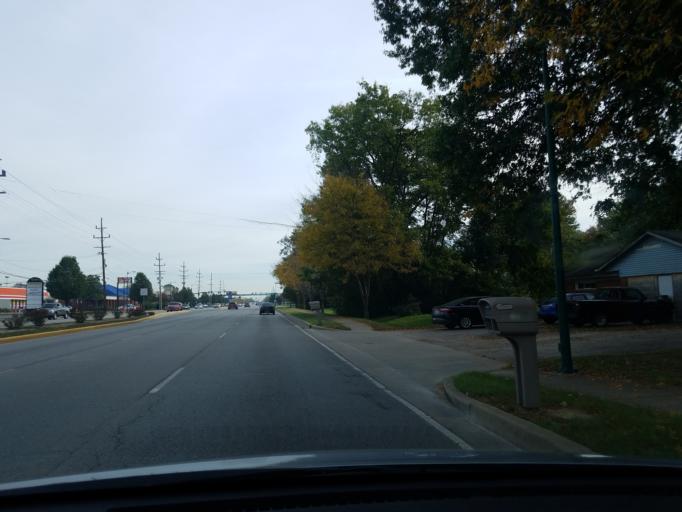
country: US
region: Indiana
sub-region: Clark County
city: Clarksville
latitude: 38.3081
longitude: -85.7725
